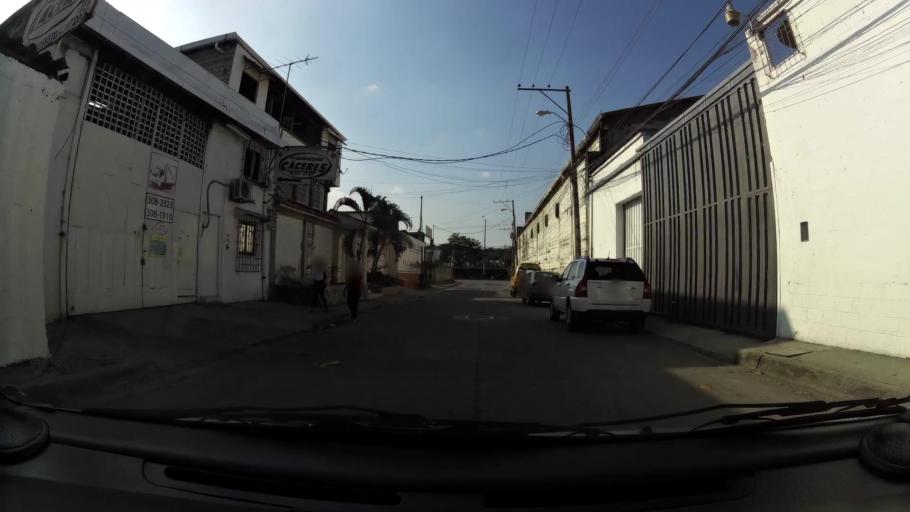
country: EC
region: Guayas
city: Guayaquil
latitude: -2.1409
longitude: -79.9301
